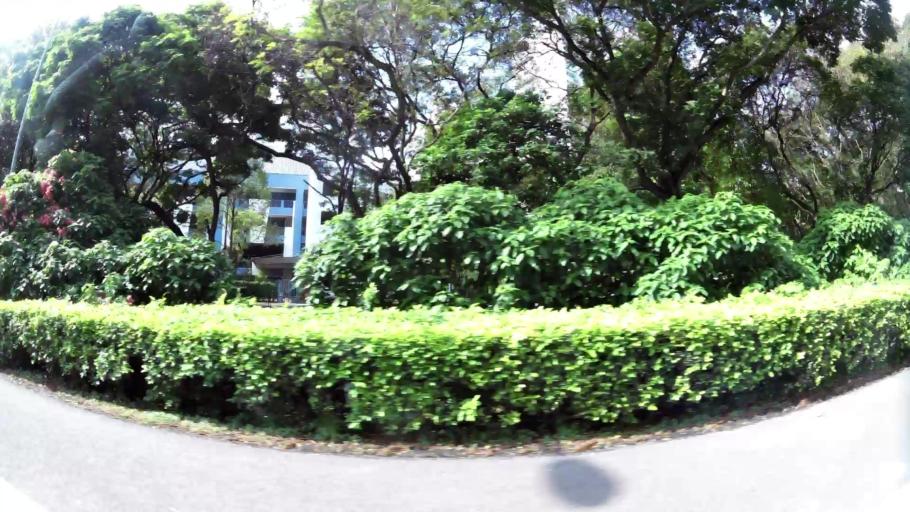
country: SG
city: Singapore
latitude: 1.2759
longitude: 103.8278
